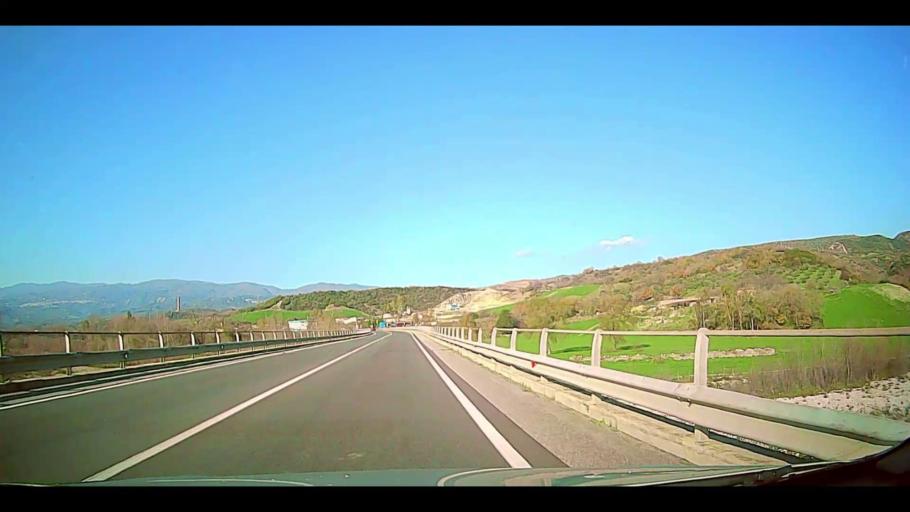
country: IT
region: Calabria
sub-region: Provincia di Crotone
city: Belvedere Spinello
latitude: 39.1880
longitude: 16.8530
